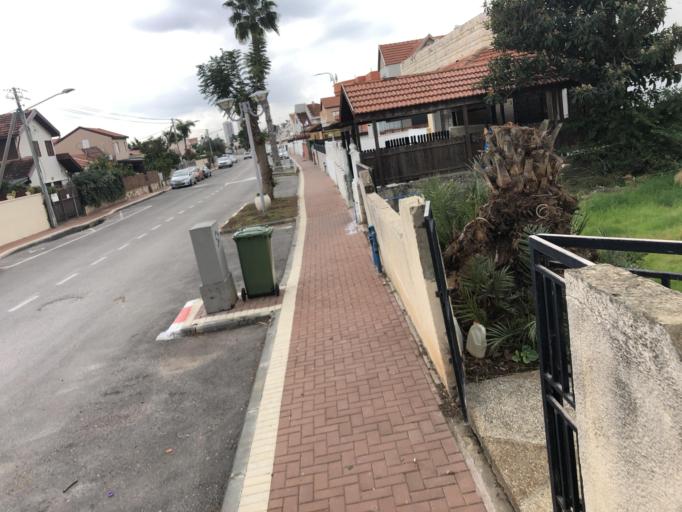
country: IL
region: Northern District
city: `Akko
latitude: 32.9351
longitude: 35.0952
